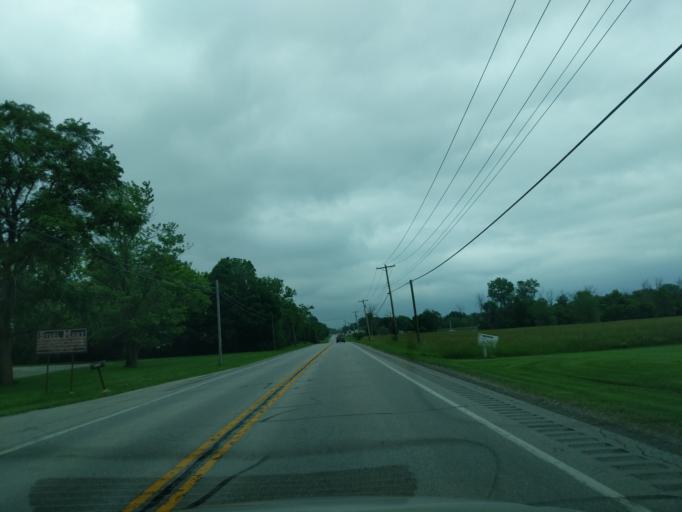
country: US
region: Indiana
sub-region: Madison County
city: Alexandria
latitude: 40.2774
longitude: -85.6841
